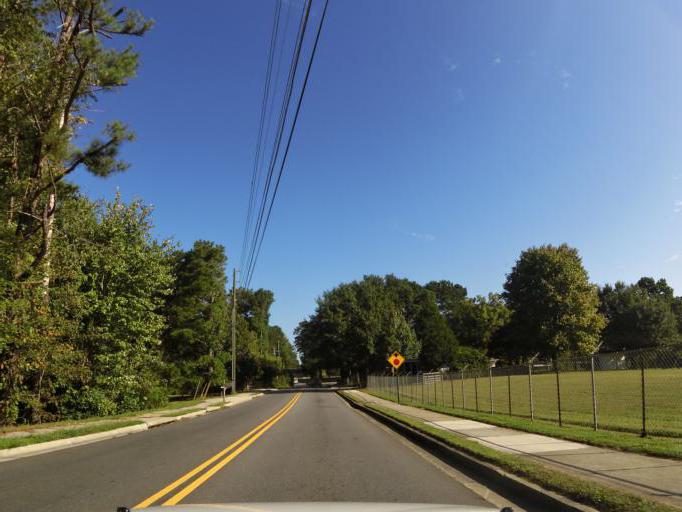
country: US
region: Georgia
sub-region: Cobb County
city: Acworth
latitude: 34.0141
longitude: -84.6757
